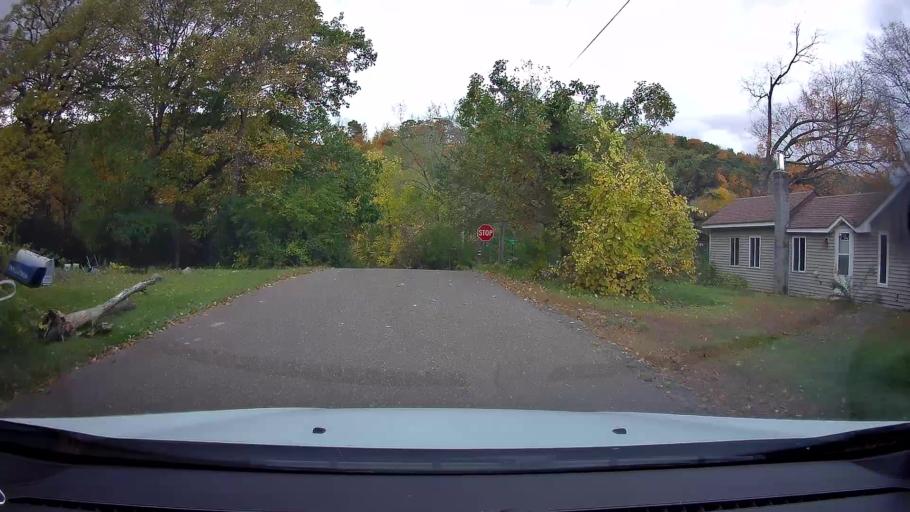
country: US
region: Wisconsin
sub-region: Polk County
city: Saint Croix Falls
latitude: 45.4078
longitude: -92.6511
